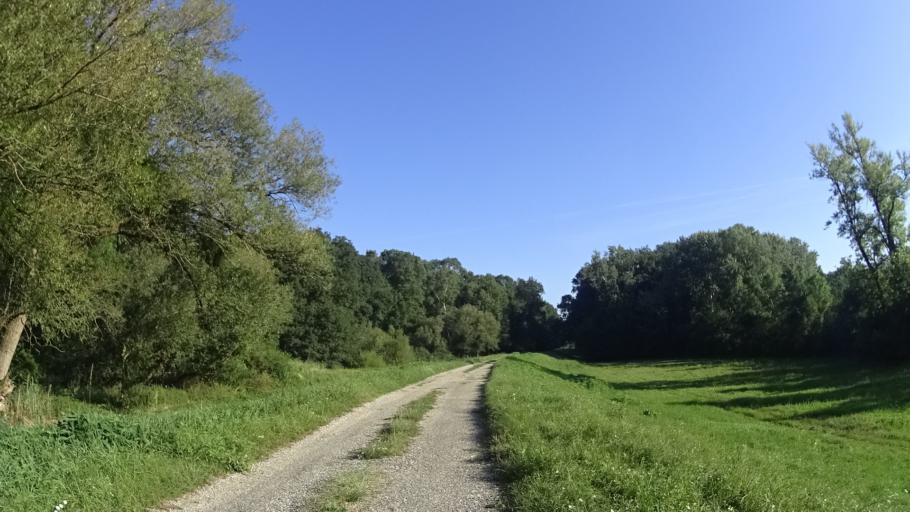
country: AT
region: Lower Austria
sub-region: Politischer Bezirk Mistelbach
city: Rabensburg
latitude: 48.6343
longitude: 16.9782
